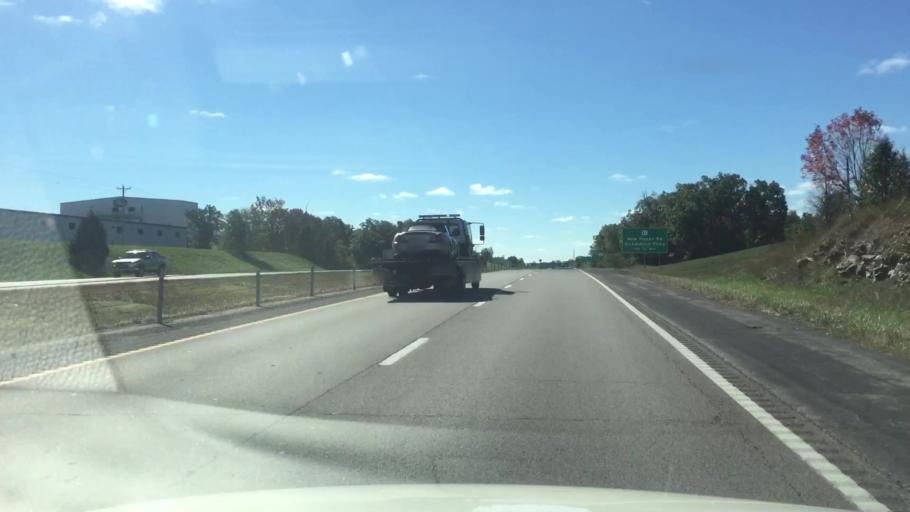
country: US
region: Missouri
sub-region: Boone County
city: Columbia
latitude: 38.9244
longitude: -92.2946
